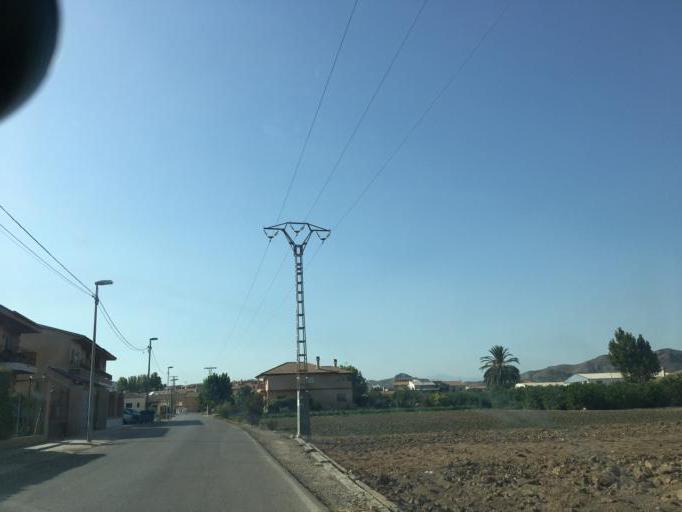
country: ES
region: Murcia
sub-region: Murcia
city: Santomera
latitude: 38.0348
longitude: -1.0728
